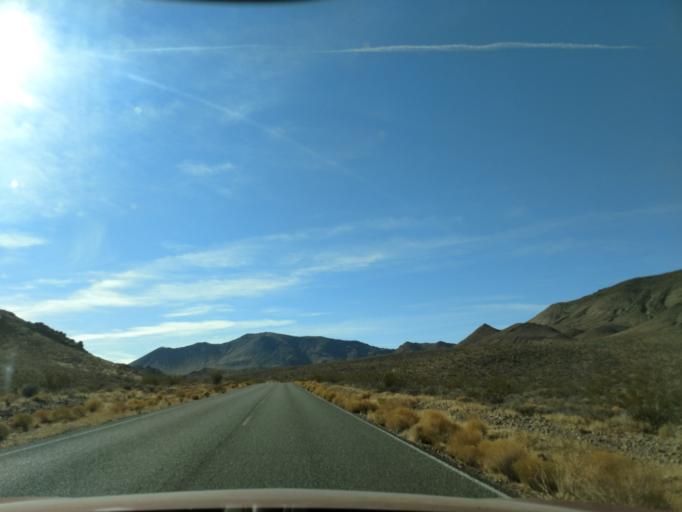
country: US
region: Nevada
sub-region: Nye County
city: Beatty
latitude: 36.8100
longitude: -116.9094
